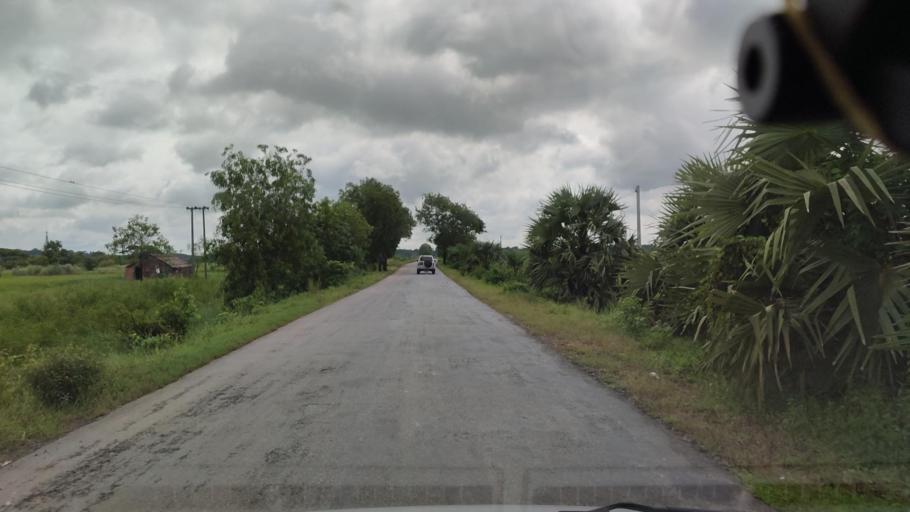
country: MM
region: Yangon
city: Kayan
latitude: 17.0965
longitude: 96.4893
